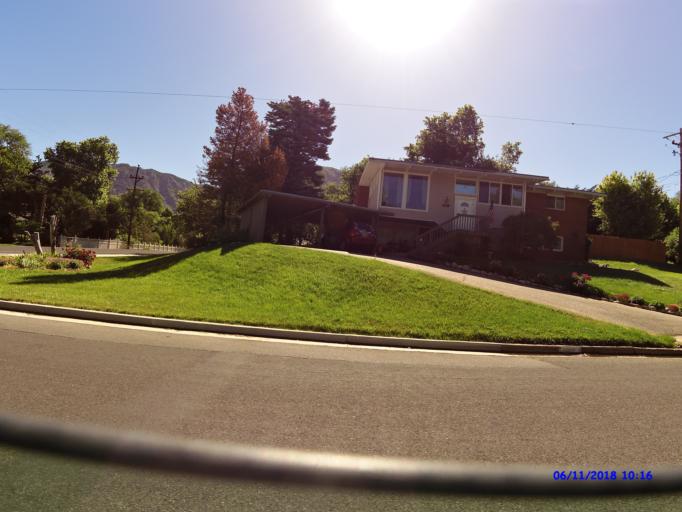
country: US
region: Utah
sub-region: Weber County
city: South Ogden
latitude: 41.2055
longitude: -111.9453
